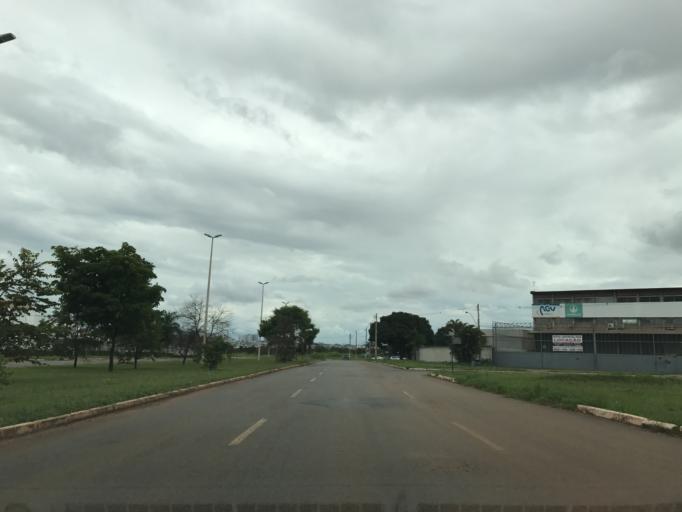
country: BR
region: Federal District
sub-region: Brasilia
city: Brasilia
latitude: -15.7942
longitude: -47.9887
